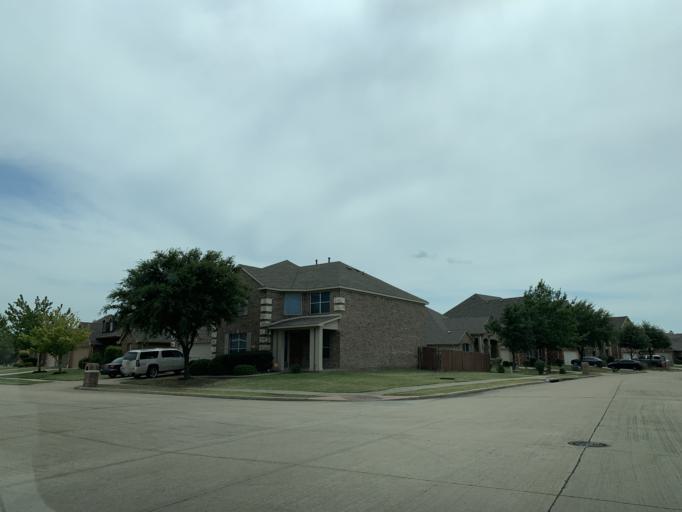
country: US
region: Texas
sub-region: Dallas County
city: Cedar Hill
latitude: 32.6488
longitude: -97.0382
